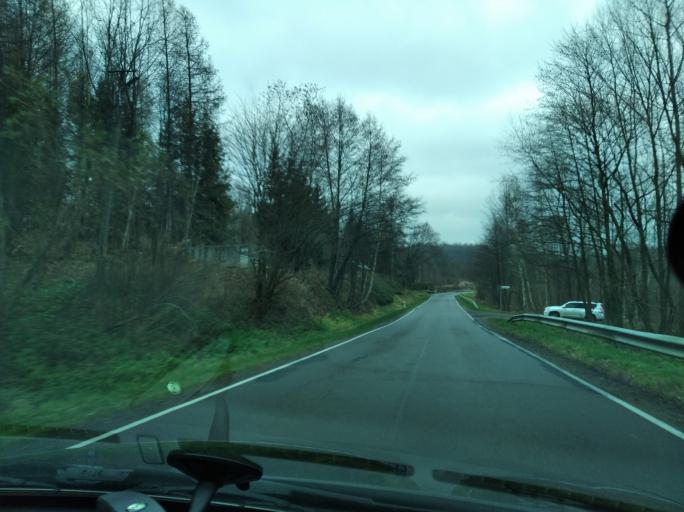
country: PL
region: Subcarpathian Voivodeship
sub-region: Powiat przeworski
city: Manasterz
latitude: 49.9204
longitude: 22.3204
